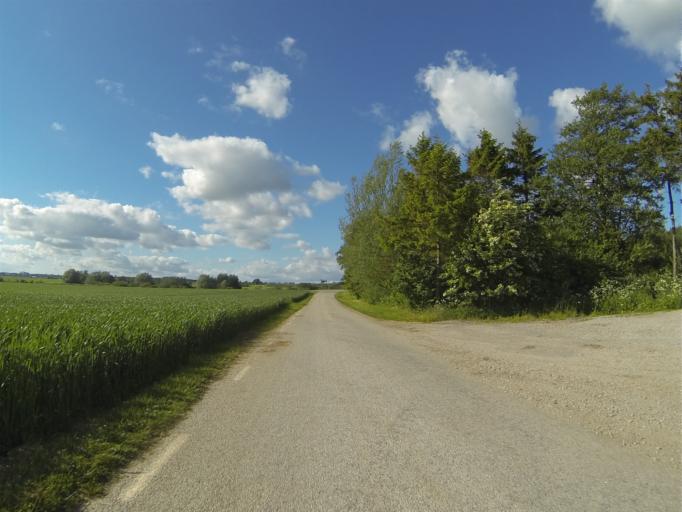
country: SE
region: Skane
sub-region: Staffanstorps Kommun
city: Staffanstorp
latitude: 55.6776
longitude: 13.2602
